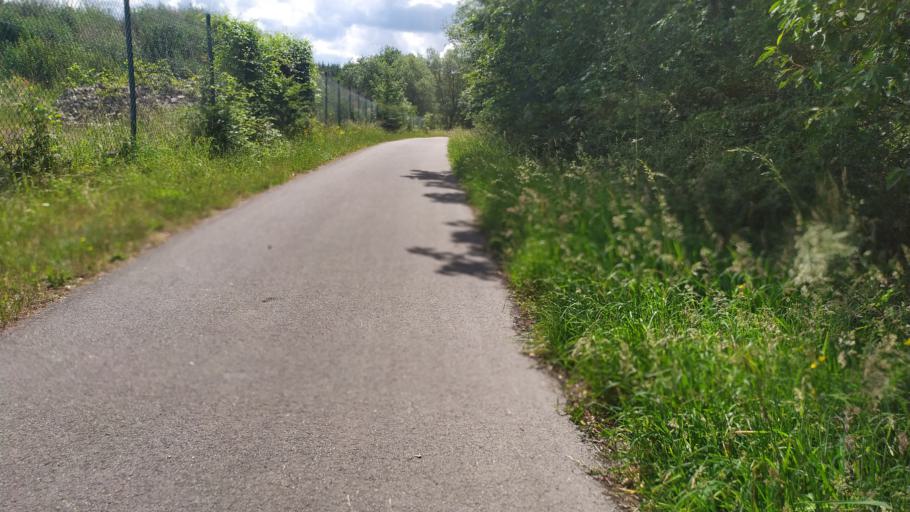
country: BE
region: Wallonia
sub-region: Province de Namur
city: Houyet
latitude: 50.1700
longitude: 5.0495
